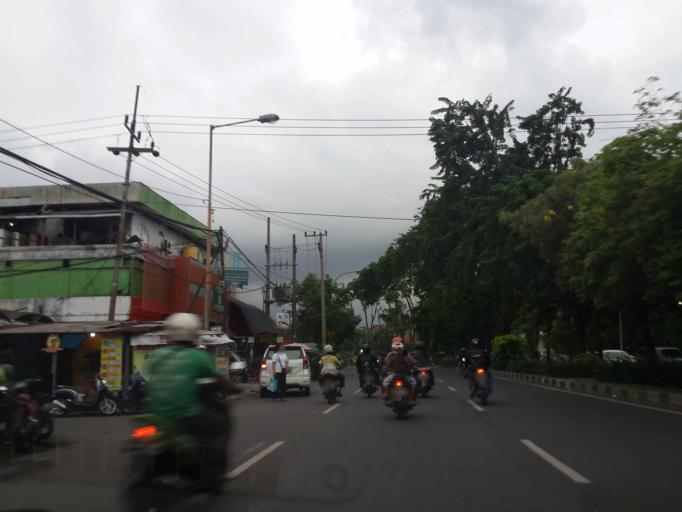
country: ID
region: East Java
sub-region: Kota Surabaya
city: Surabaya
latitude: -7.2627
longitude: 112.7267
